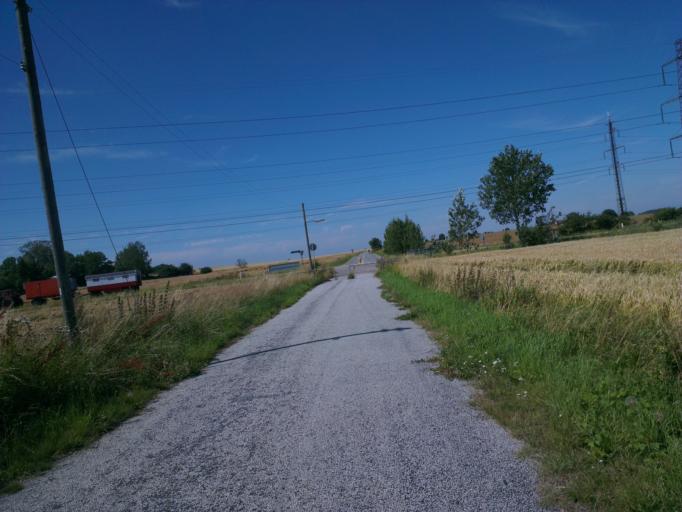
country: DK
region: Capital Region
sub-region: Frederikssund Kommune
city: Slangerup
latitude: 55.8540
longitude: 12.1611
